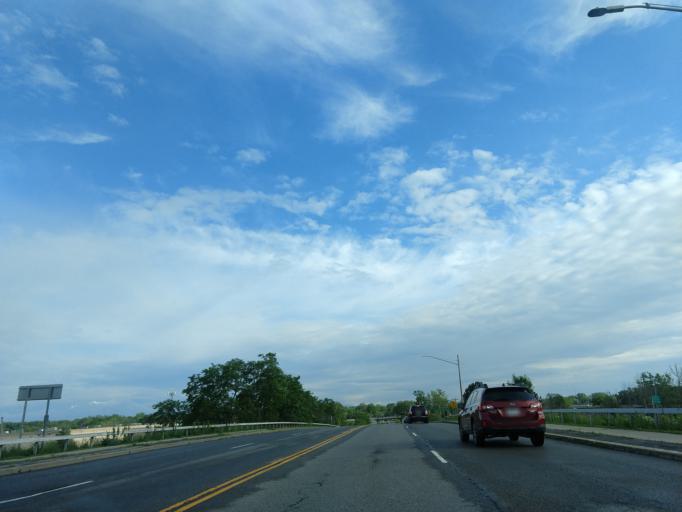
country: US
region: New York
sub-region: Erie County
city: West Seneca
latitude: 42.8543
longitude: -78.7878
